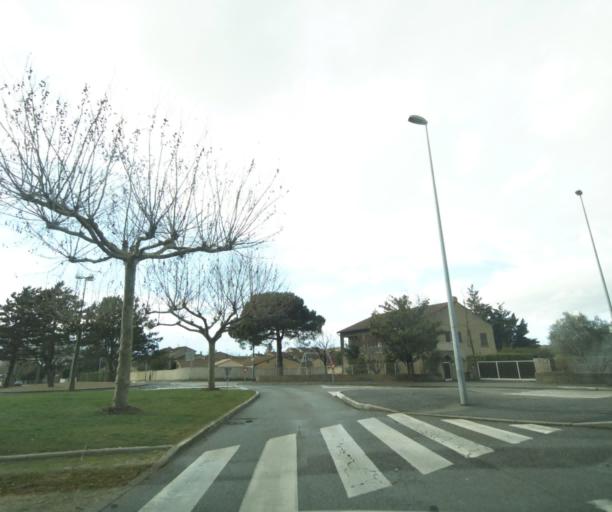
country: FR
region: Rhone-Alpes
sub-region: Departement de la Drome
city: Bourg-les-Valence
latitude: 44.9567
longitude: 4.9091
